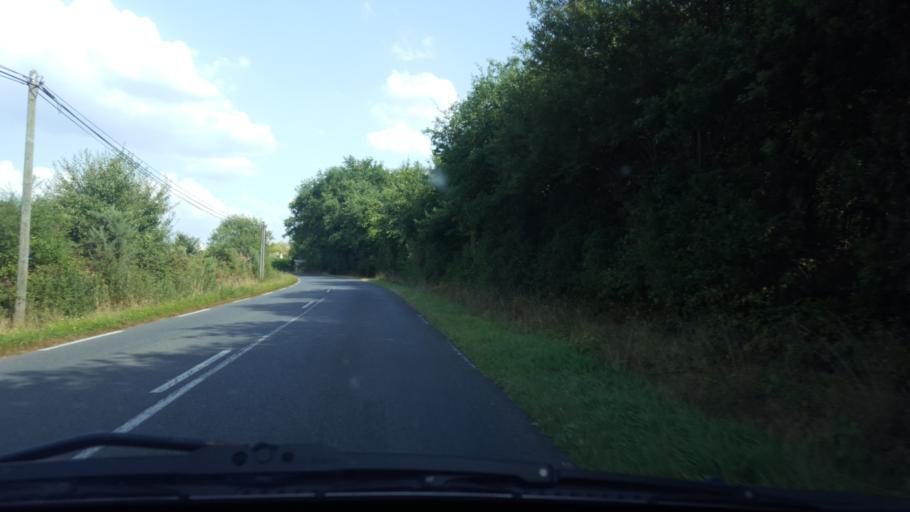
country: FR
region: Pays de la Loire
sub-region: Departement de la Loire-Atlantique
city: Geneston
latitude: 47.0605
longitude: -1.5457
